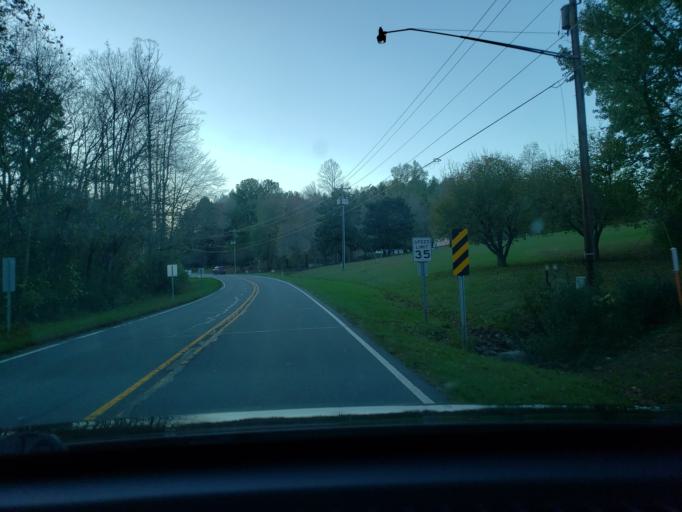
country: US
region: North Carolina
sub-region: Stokes County
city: Danbury
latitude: 36.4120
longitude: -80.2158
